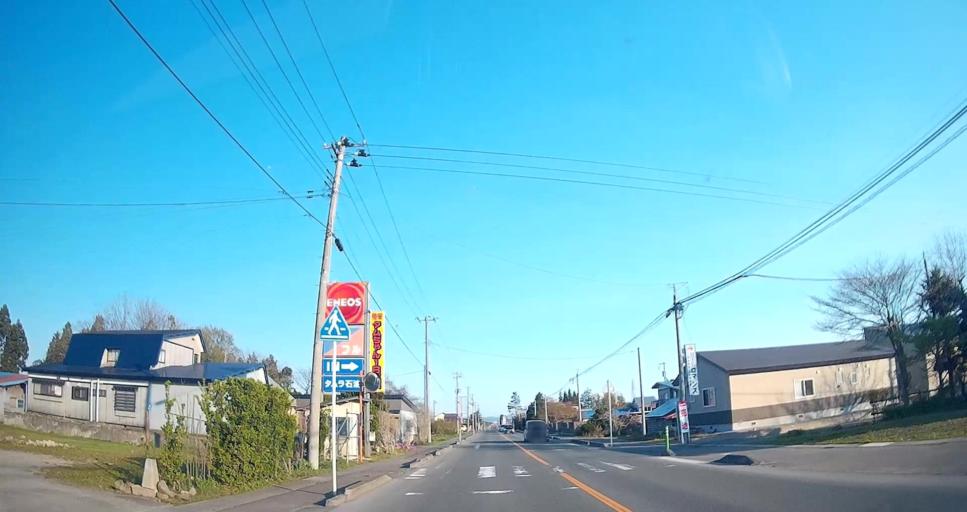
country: JP
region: Aomori
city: Mutsu
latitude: 41.2667
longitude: 141.2214
